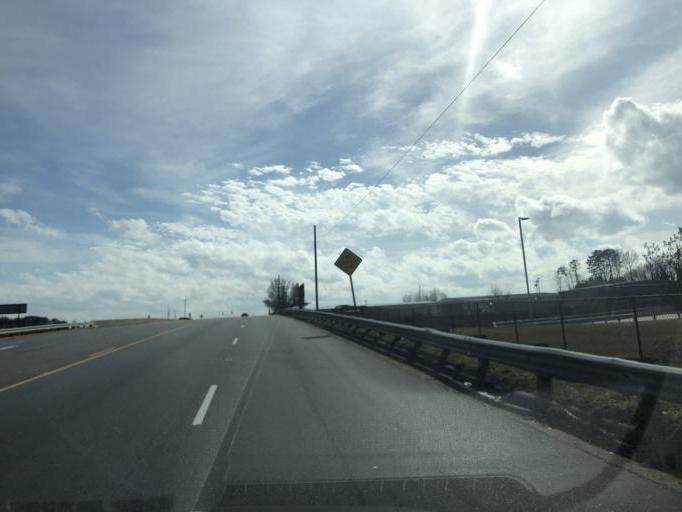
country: US
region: North Carolina
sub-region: Gaston County
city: Lowell
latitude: 35.2612
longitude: -81.1049
